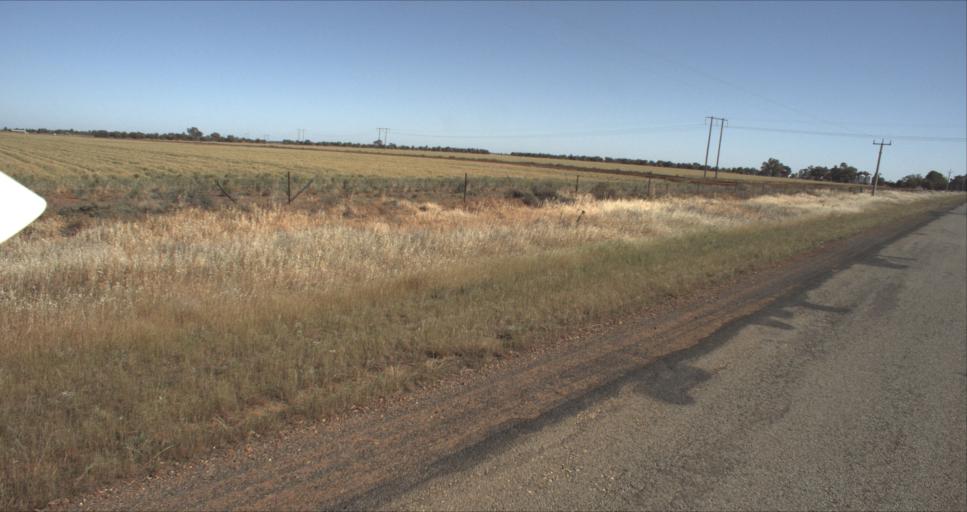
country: AU
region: New South Wales
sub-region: Leeton
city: Leeton
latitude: -34.5610
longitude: 146.2654
